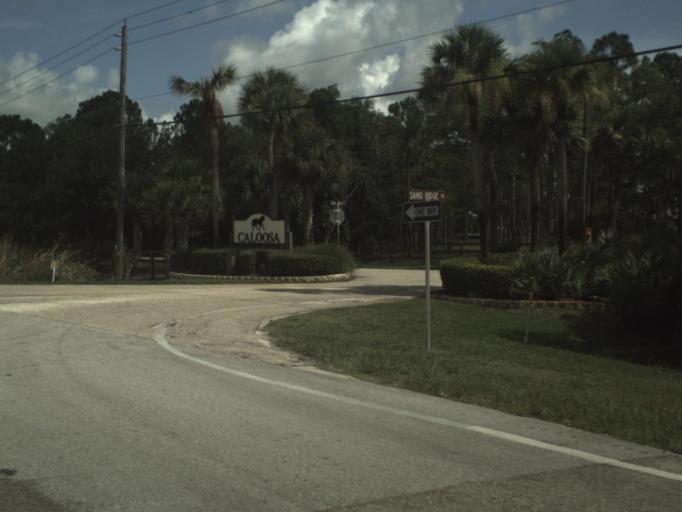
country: US
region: Florida
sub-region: Palm Beach County
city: Palm Beach Gardens
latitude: 26.8670
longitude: -80.2376
